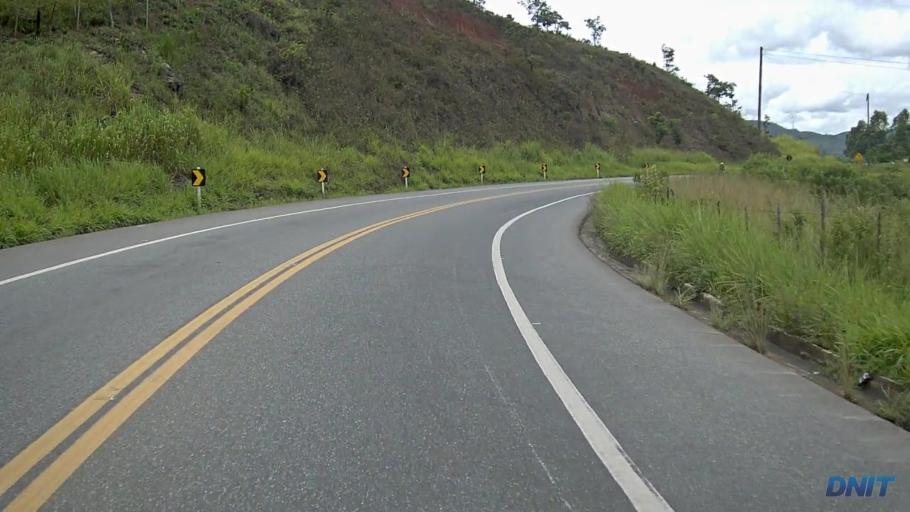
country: BR
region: Minas Gerais
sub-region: Nova Era
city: Nova Era
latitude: -19.6859
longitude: -42.9832
